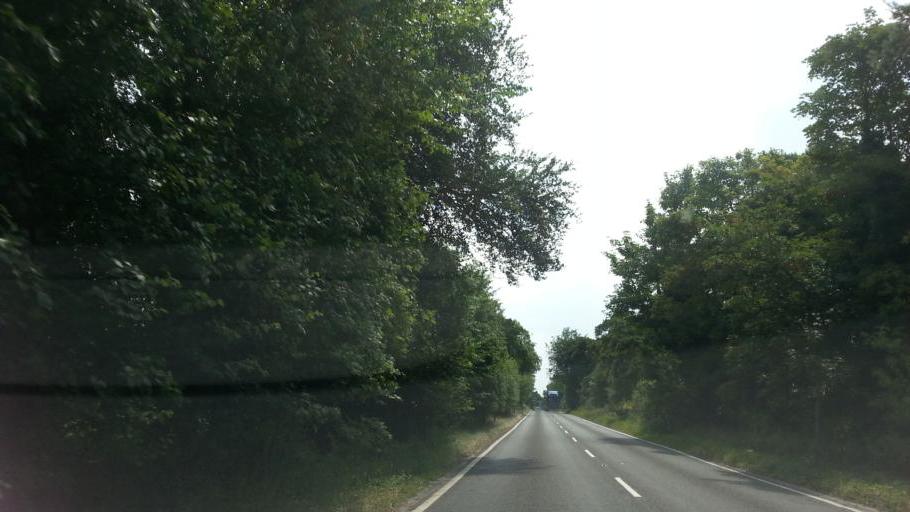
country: GB
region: England
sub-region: Suffolk
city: Lakenheath
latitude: 52.3636
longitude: 0.5396
